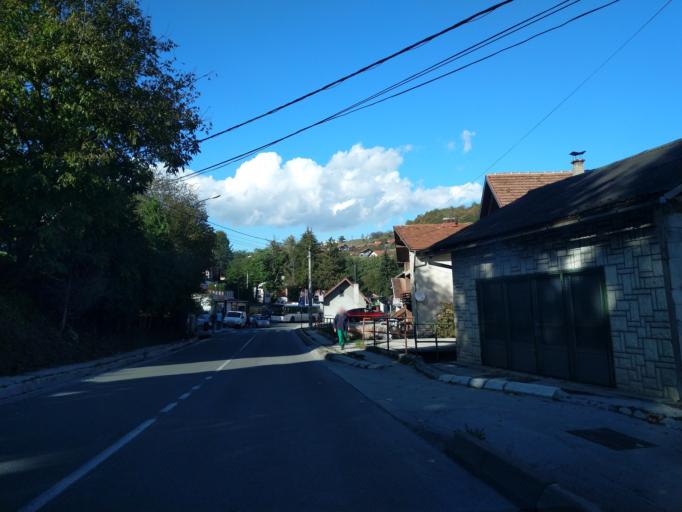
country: RS
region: Central Serbia
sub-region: Zlatiborski Okrug
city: Uzice
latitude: 43.8625
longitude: 19.8245
